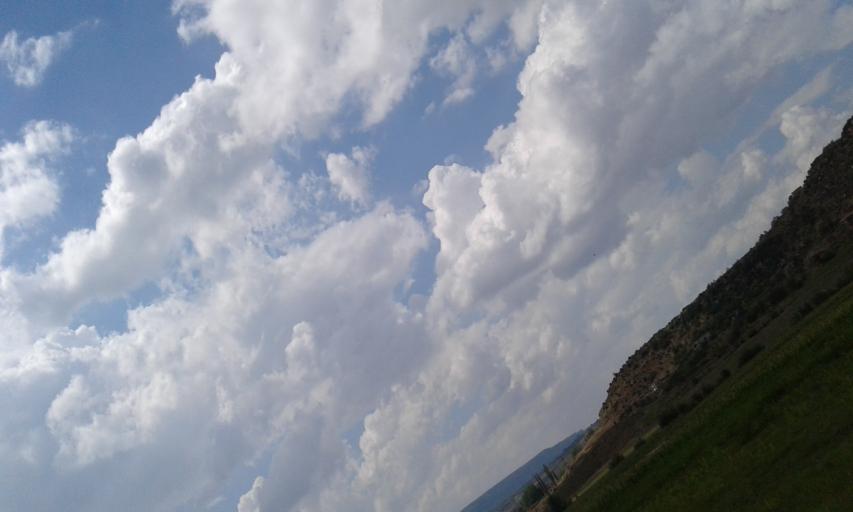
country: LS
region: Maseru
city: Maseru
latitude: -29.4124
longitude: 27.5676
